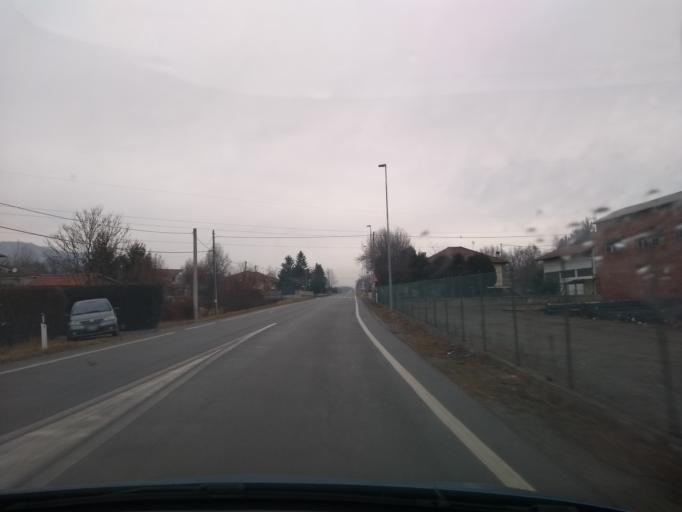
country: IT
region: Piedmont
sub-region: Provincia di Torino
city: Busano
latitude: 45.3347
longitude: 7.6545
